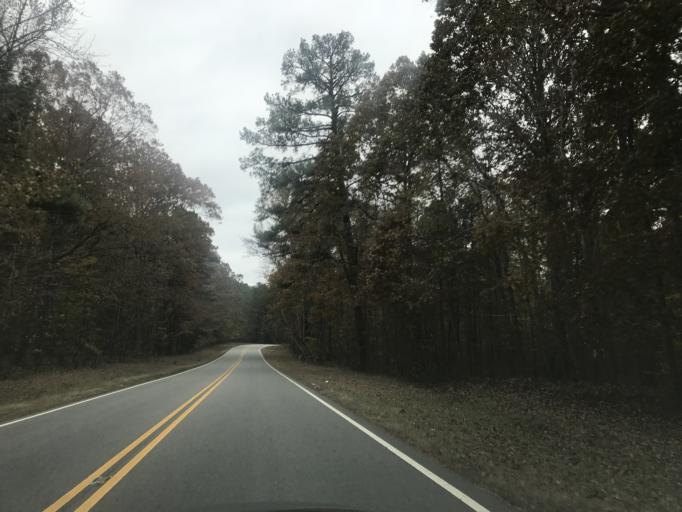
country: US
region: North Carolina
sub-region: Franklin County
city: Youngsville
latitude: 36.0091
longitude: -78.4907
